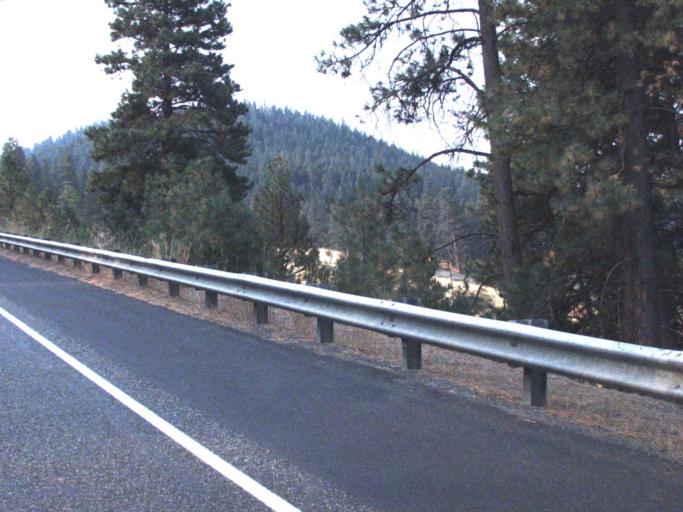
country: US
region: Washington
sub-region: Kittitas County
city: Cle Elum
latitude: 47.1970
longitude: -120.7068
